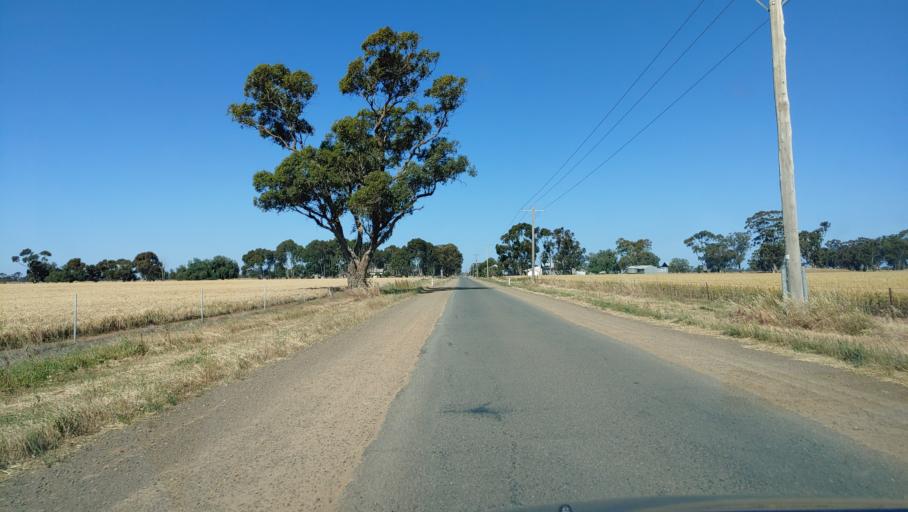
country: AU
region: Victoria
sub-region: Greater Bendigo
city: Long Gully
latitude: -36.6037
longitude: 144.0923
